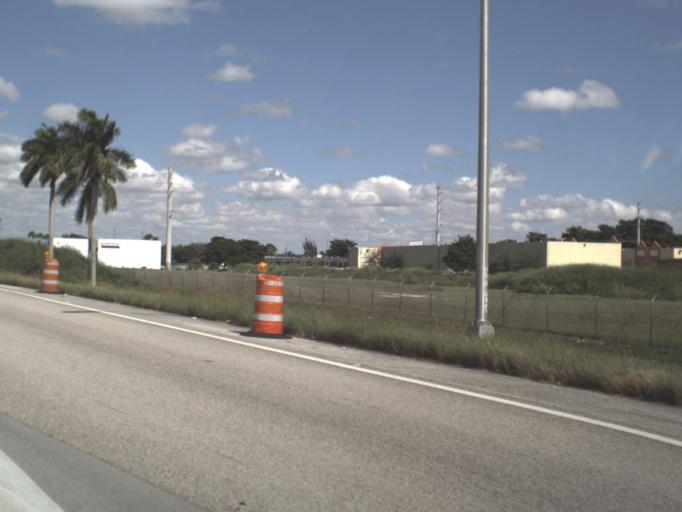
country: US
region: Florida
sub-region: Miami-Dade County
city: South Miami Heights
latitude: 25.5920
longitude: -80.3693
